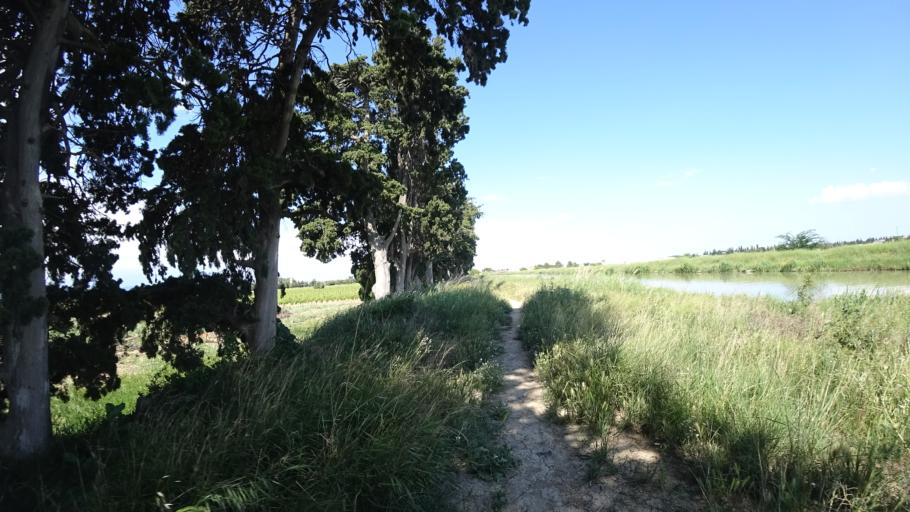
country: FR
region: Languedoc-Roussillon
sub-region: Departement de l'Aude
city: Ginestas
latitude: 43.2604
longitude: 2.9001
